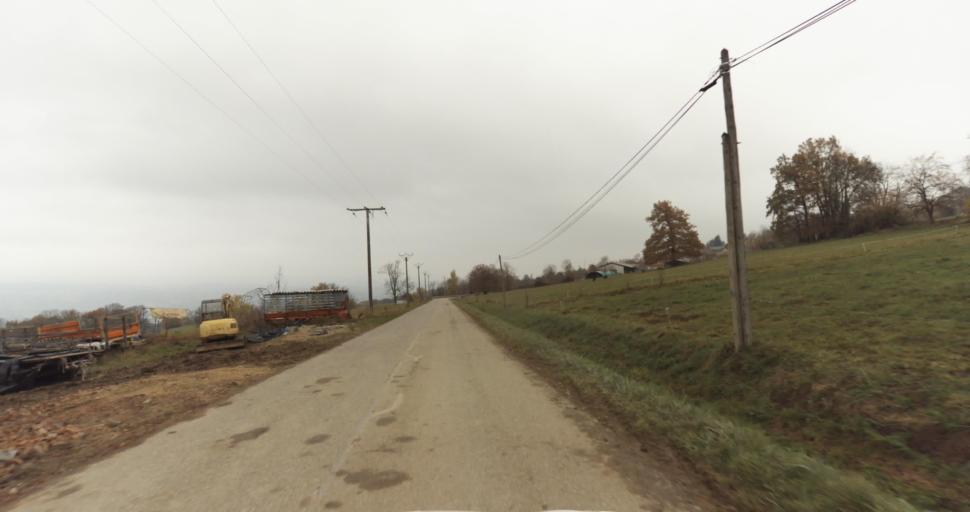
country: FR
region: Rhone-Alpes
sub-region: Departement de la Haute-Savoie
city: Saint-Felix
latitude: 45.7697
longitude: 5.9865
